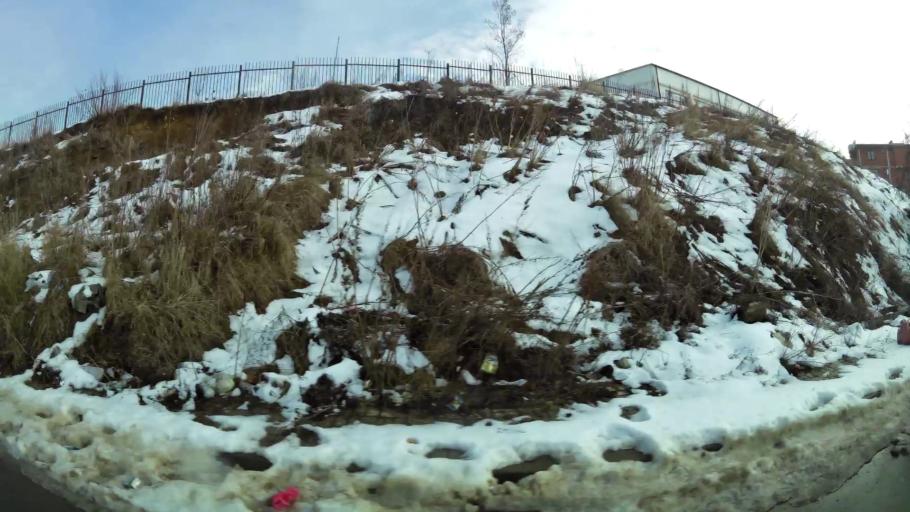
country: XK
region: Pristina
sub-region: Komuna e Prishtines
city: Pristina
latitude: 42.6875
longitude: 21.1555
